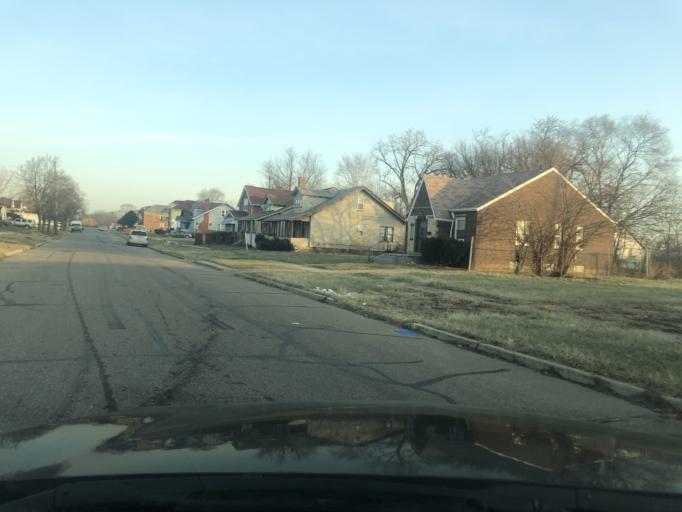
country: US
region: Michigan
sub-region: Wayne County
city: Highland Park
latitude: 42.3990
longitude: -83.1319
